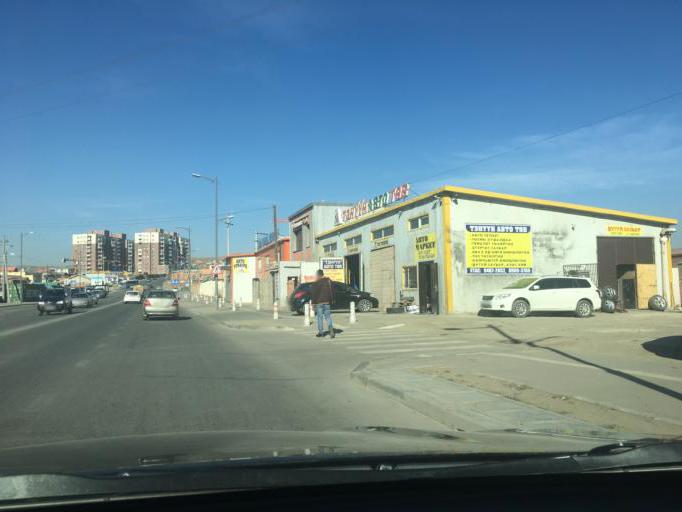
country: MN
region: Ulaanbaatar
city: Ulaanbaatar
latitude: 47.9123
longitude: 106.7832
